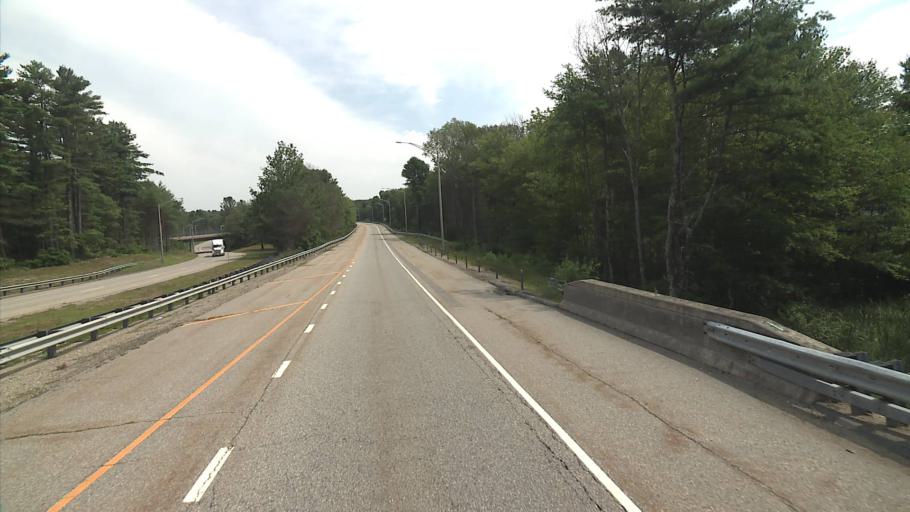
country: US
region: Rhode Island
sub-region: Providence County
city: Foster
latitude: 41.7905
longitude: -71.7990
